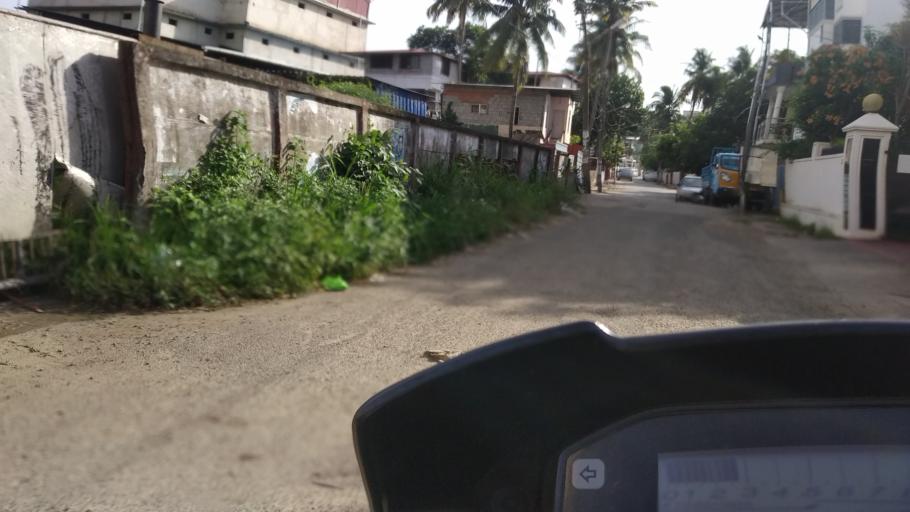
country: IN
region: Kerala
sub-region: Ernakulam
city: Elur
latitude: 10.0067
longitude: 76.2972
